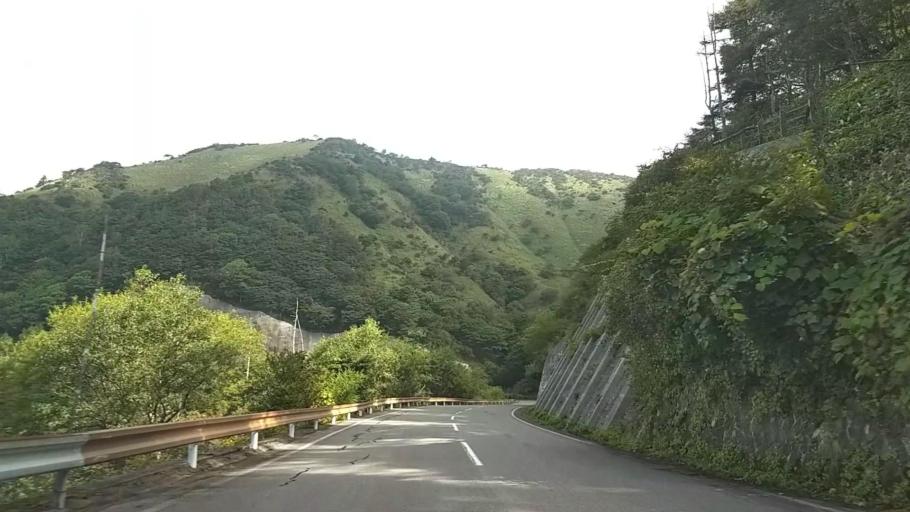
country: JP
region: Nagano
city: Suwa
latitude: 36.1261
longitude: 138.1532
